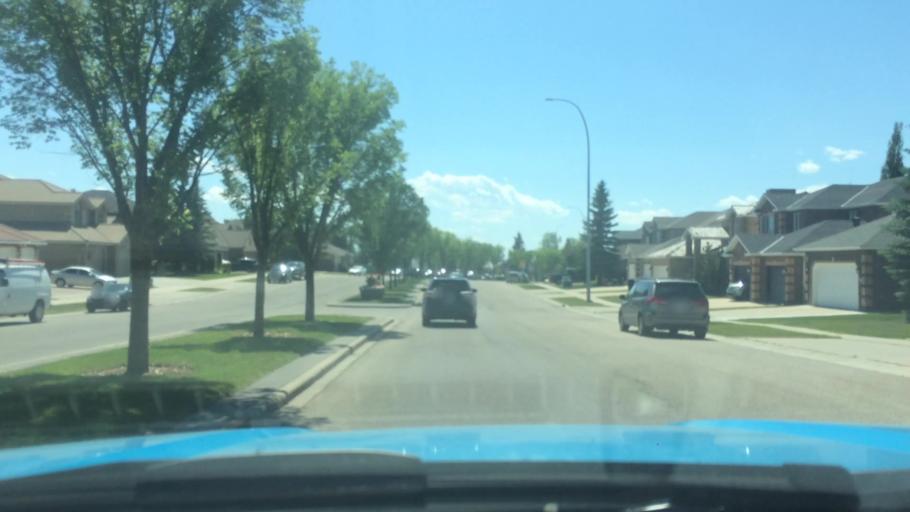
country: CA
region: Alberta
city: Calgary
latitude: 51.1353
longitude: -114.2018
